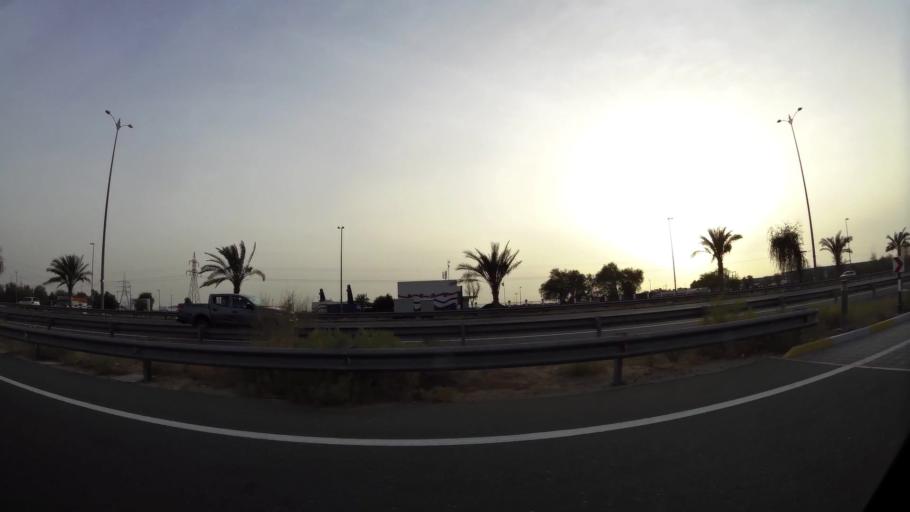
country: OM
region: Al Buraimi
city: Al Buraymi
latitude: 24.3986
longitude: 55.7965
